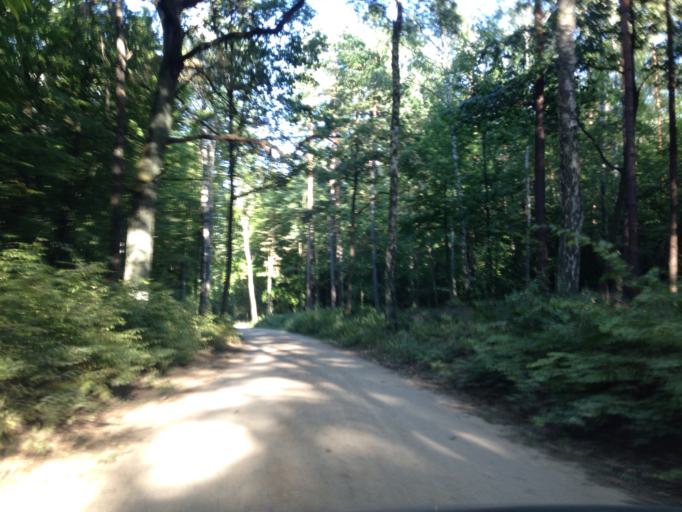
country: PL
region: Kujawsko-Pomorskie
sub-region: Powiat brodnicki
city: Gorzno
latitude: 53.1804
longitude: 19.6597
